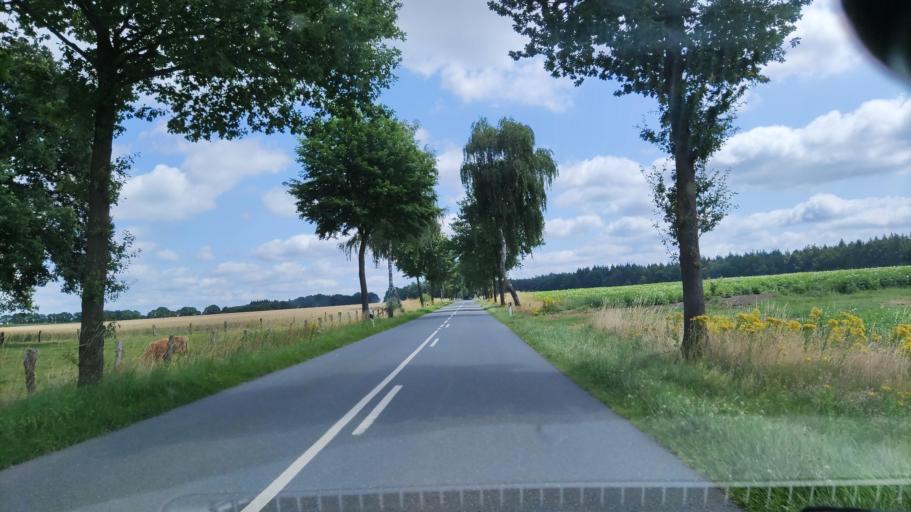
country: DE
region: Lower Saxony
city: Bad Fallingbostel
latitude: 52.8292
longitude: 9.6501
